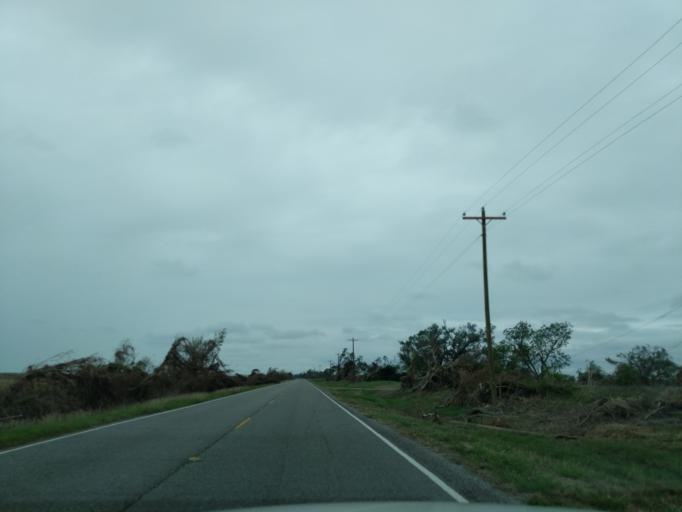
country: US
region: Louisiana
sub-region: Cameron Parish
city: Cameron
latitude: 29.7865
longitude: -93.1240
